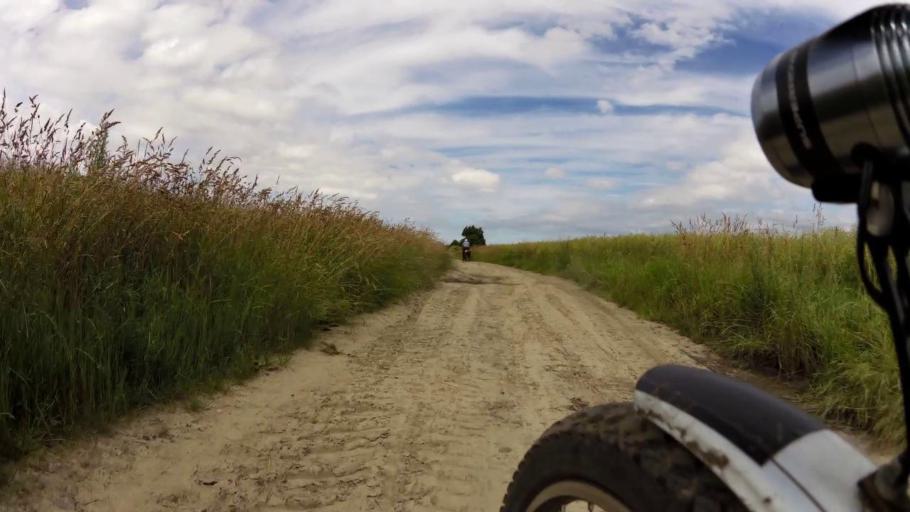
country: PL
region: West Pomeranian Voivodeship
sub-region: Powiat bialogardzki
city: Bialogard
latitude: 53.9741
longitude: 15.9986
